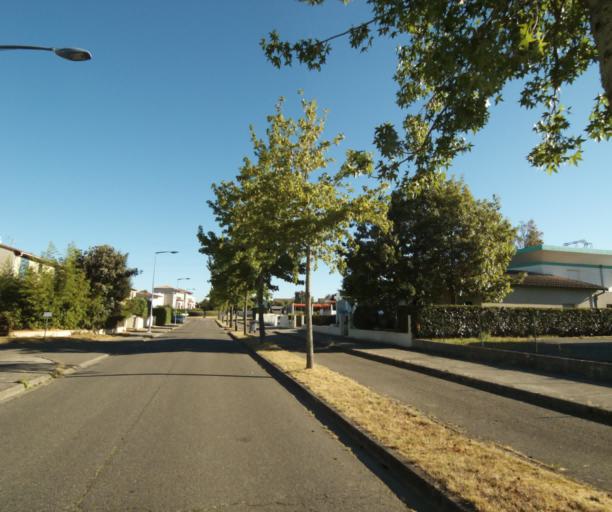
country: FR
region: Midi-Pyrenees
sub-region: Departement de la Haute-Garonne
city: Castanet-Tolosan
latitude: 43.5200
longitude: 1.5117
